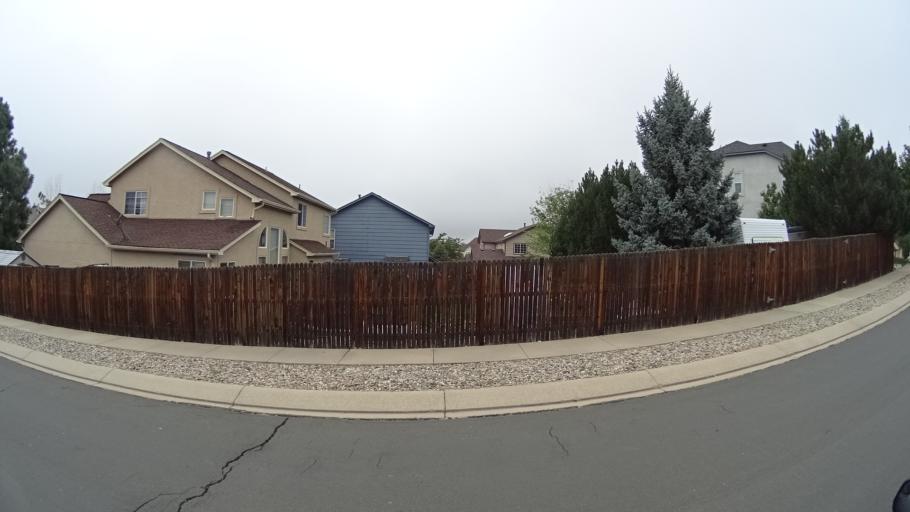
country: US
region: Colorado
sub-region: El Paso County
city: Cimarron Hills
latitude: 38.9312
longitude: -104.7491
